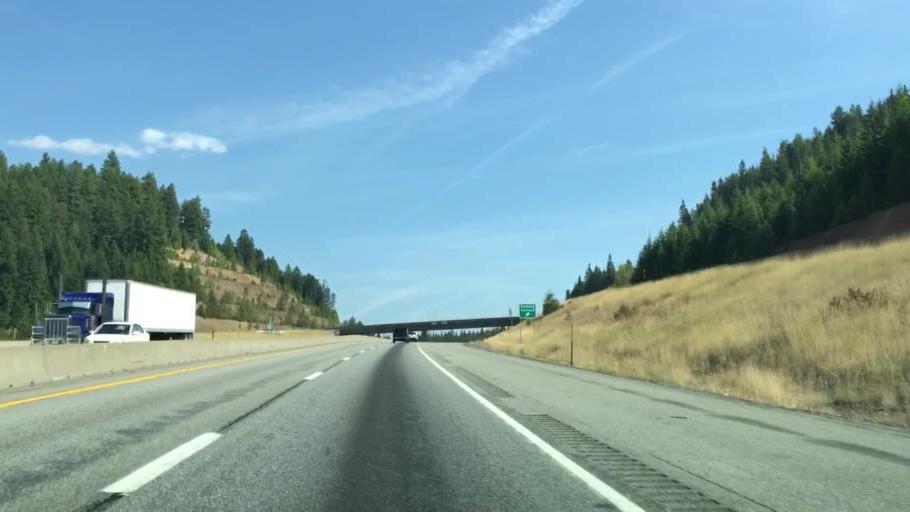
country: US
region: Idaho
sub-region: Kootenai County
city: Coeur d'Alene
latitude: 47.6228
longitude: -116.5283
